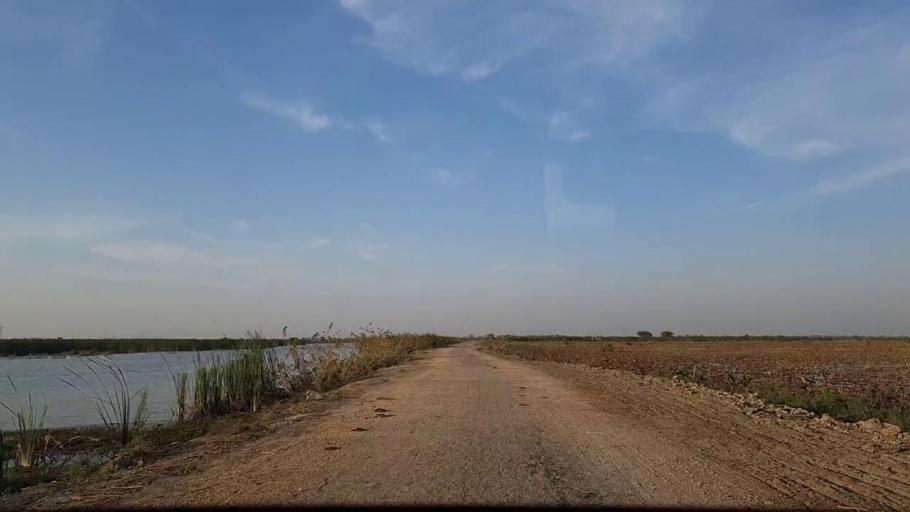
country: PK
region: Sindh
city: Mirpur Batoro
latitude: 24.6550
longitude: 68.1464
